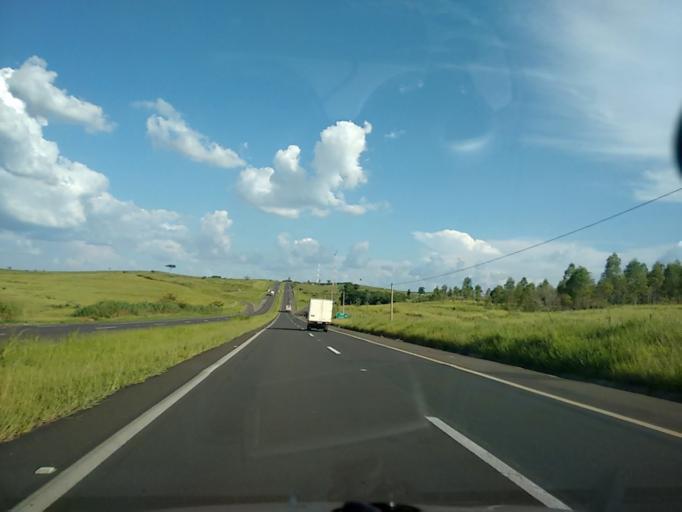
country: BR
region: Sao Paulo
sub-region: Duartina
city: Duartina
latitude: -22.2779
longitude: -49.4993
